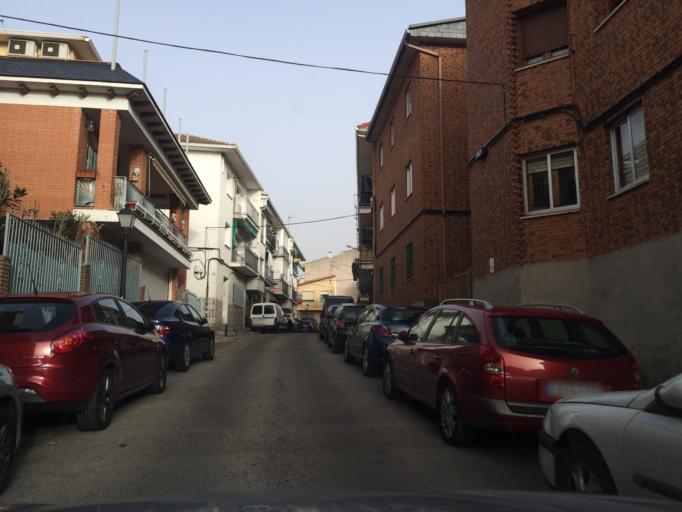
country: ES
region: Madrid
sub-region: Provincia de Madrid
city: Manzanares el Real
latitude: 40.7277
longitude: -3.8659
